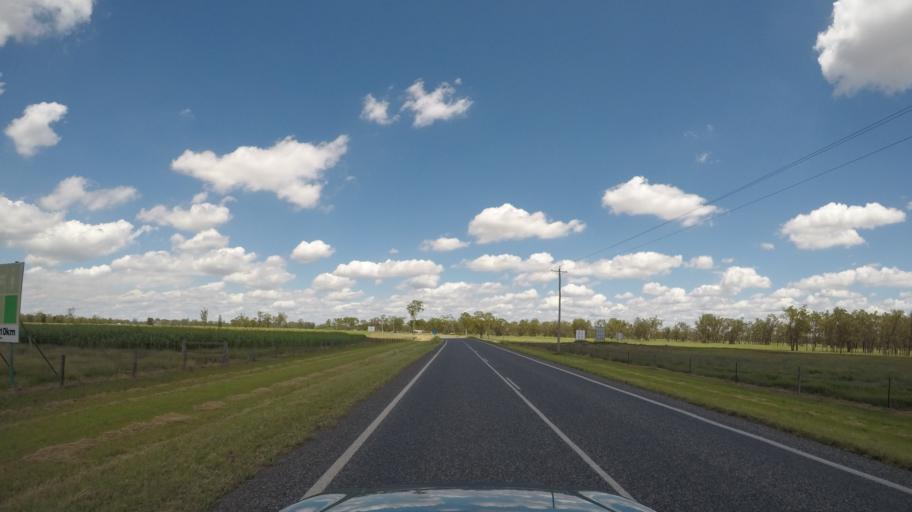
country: AU
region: Queensland
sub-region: Toowoomba
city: Oakey
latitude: -27.8737
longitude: 151.2437
